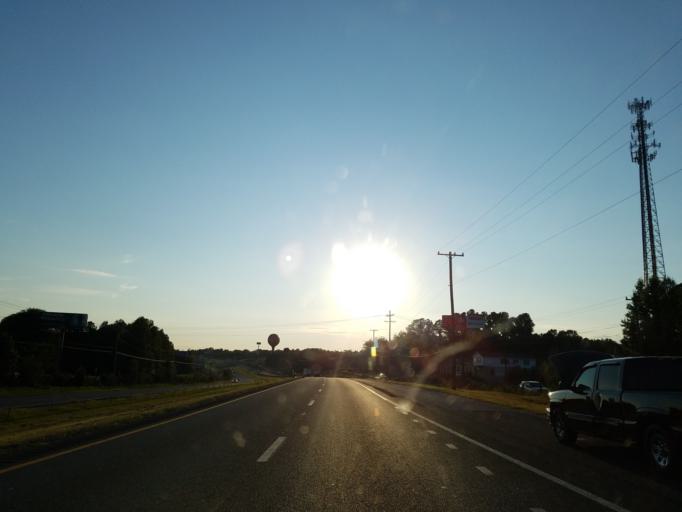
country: US
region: South Carolina
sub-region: Cherokee County
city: Gaffney
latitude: 35.0974
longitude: -81.6755
